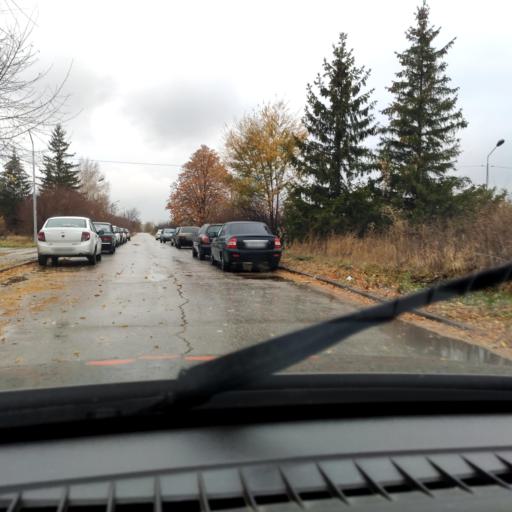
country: RU
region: Samara
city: Tol'yatti
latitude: 53.5531
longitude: 49.2771
